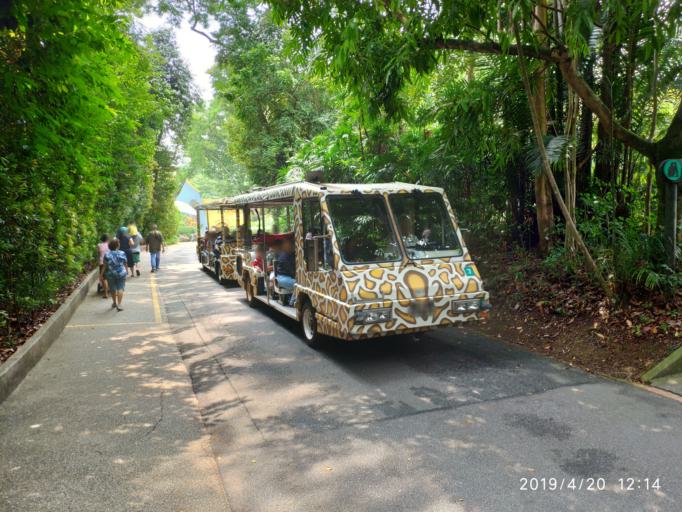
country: MY
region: Johor
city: Johor Bahru
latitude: 1.4030
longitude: 103.7958
